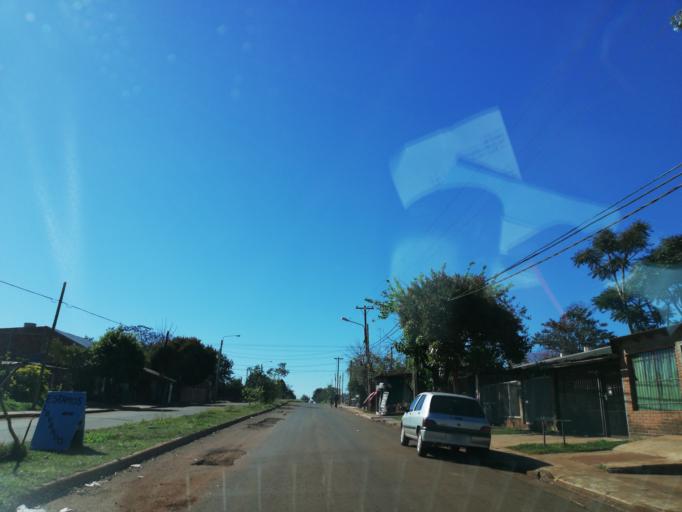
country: AR
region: Misiones
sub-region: Departamento de Capital
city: Posadas
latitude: -27.3926
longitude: -55.9476
